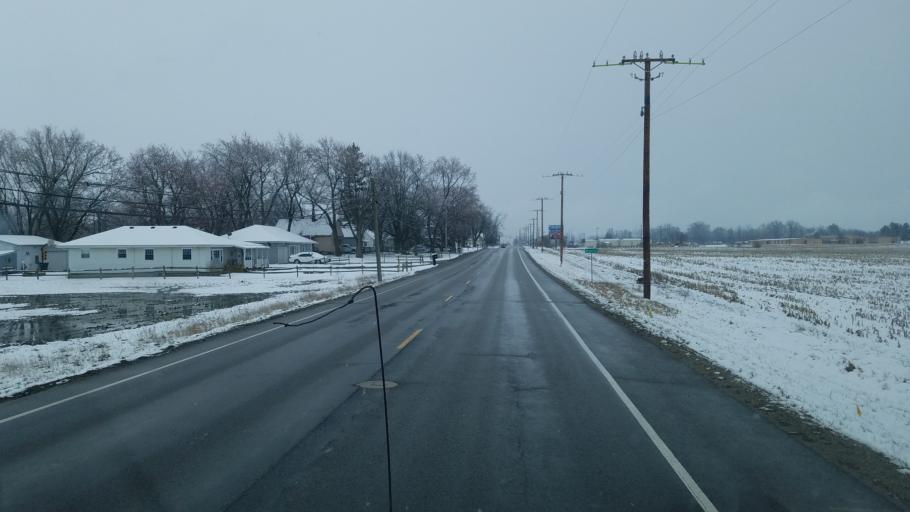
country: US
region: Indiana
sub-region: Delaware County
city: Eaton
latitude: 40.2671
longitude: -85.3681
